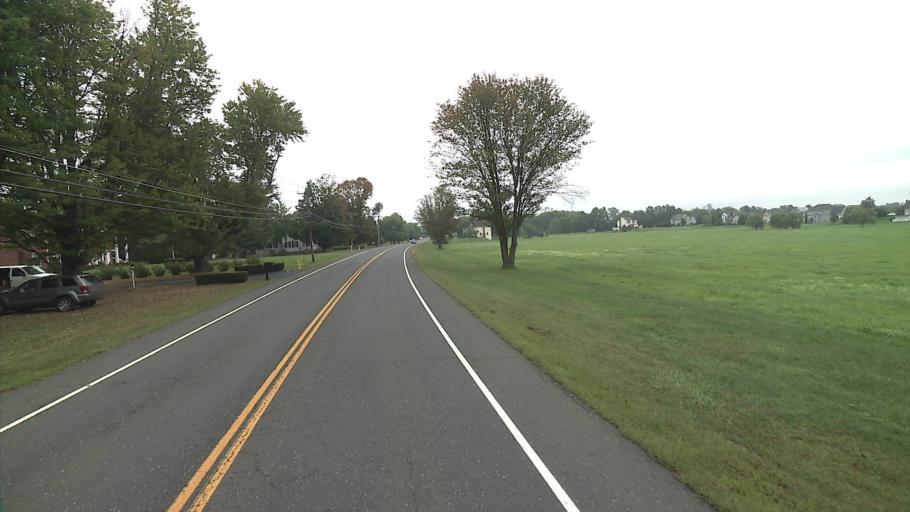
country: US
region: Connecticut
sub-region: Hartford County
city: Suffield Depot
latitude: 42.0049
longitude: -72.6448
